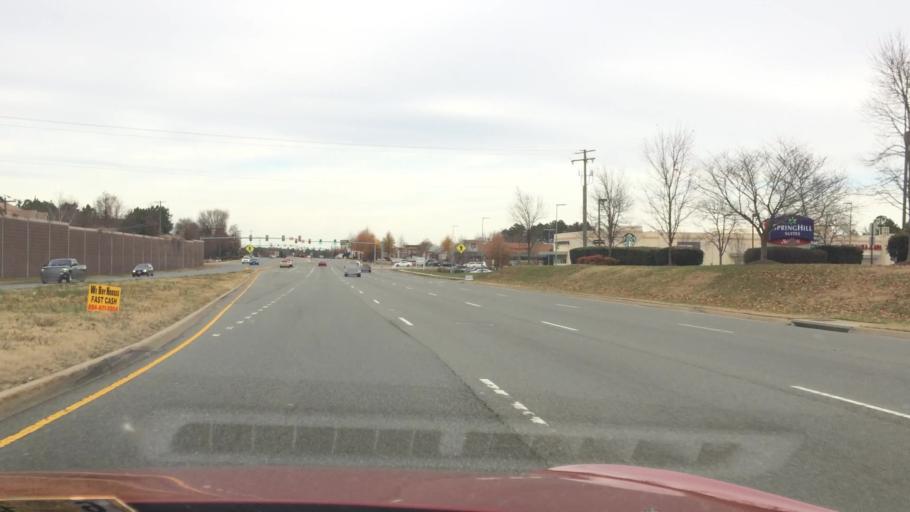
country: US
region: Virginia
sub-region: Henrico County
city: Glen Allen
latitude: 37.6641
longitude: -77.4603
